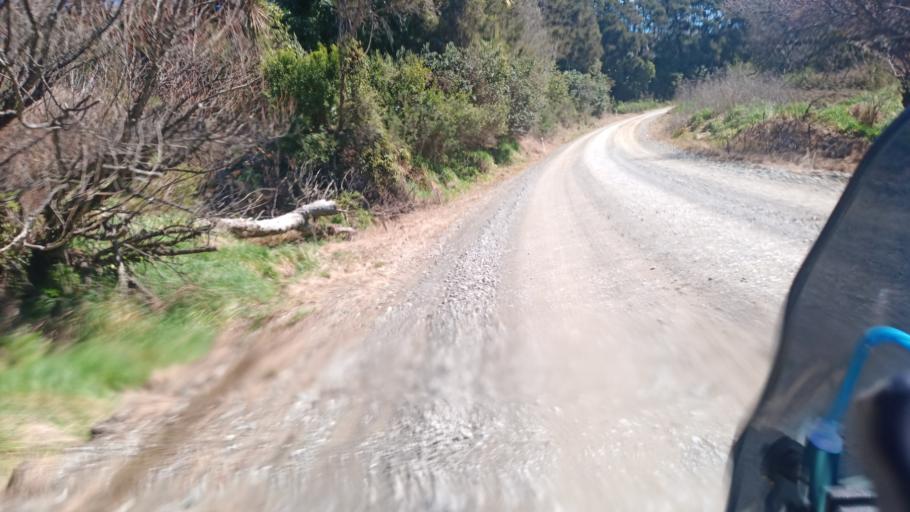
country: NZ
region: Gisborne
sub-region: Gisborne District
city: Gisborne
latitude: -37.9924
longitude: 178.2949
